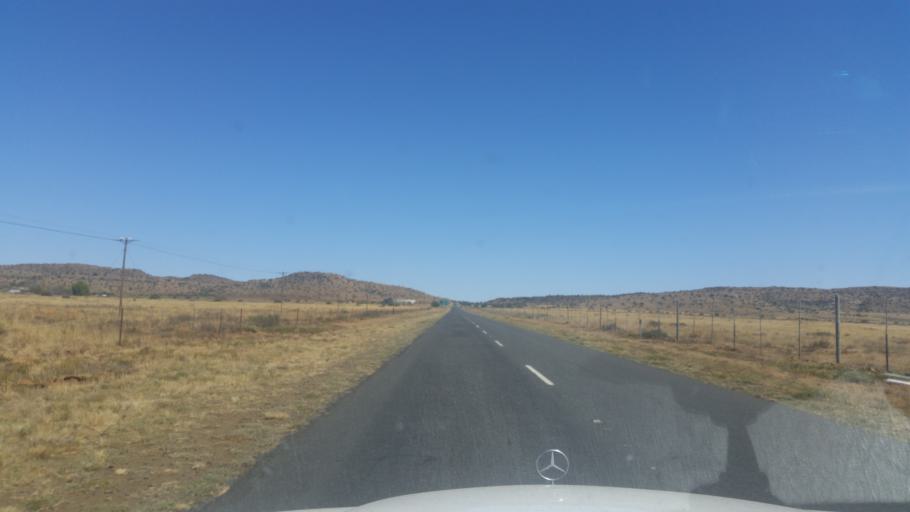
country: ZA
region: Eastern Cape
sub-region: Joe Gqabi District Municipality
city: Burgersdorp
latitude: -30.7815
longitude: 25.7681
